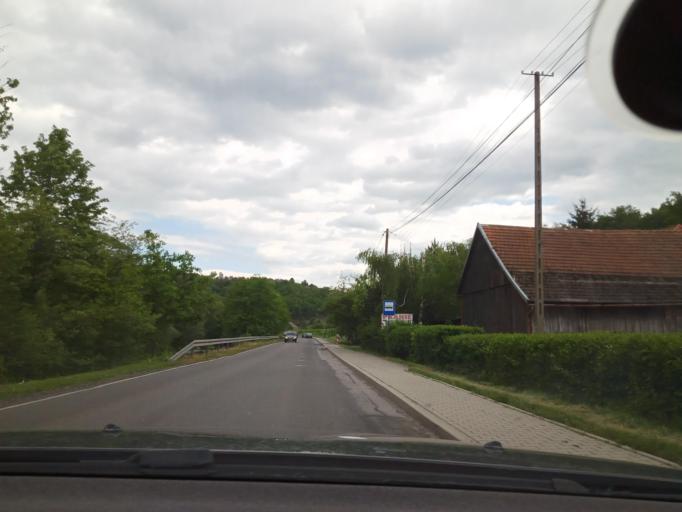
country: PL
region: Lesser Poland Voivodeship
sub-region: Powiat limanowski
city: Tymbark
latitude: 49.7495
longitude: 20.3624
